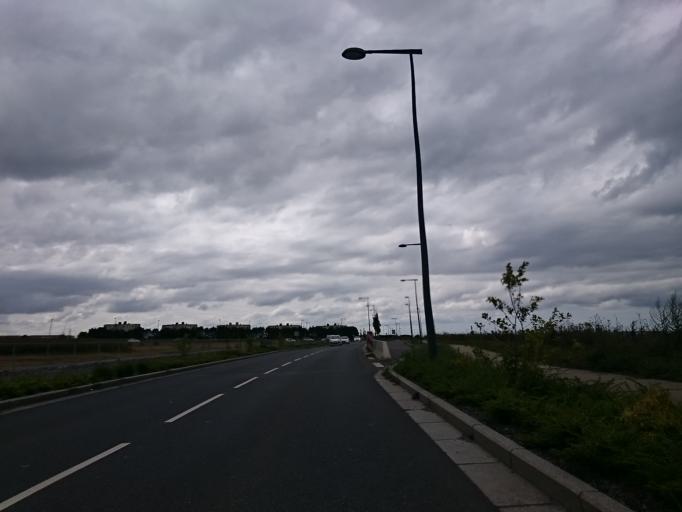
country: FR
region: Lower Normandy
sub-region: Departement du Calvados
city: Fleury-sur-Orne
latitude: 49.1428
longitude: -0.3696
